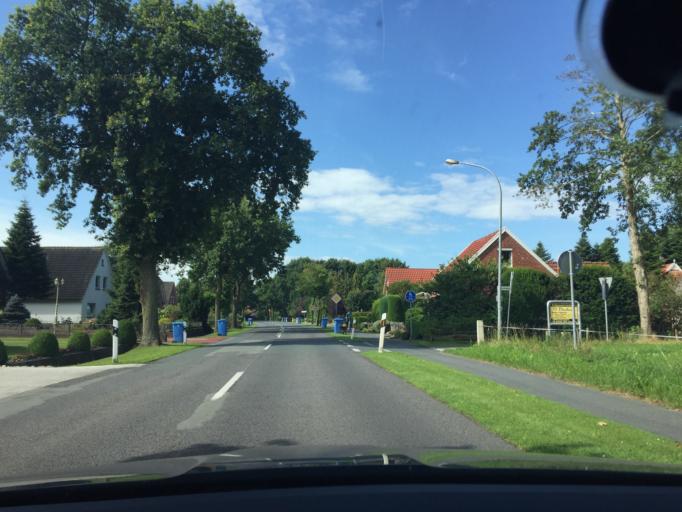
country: DE
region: Lower Saxony
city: Rechtsupweg
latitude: 53.5108
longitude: 7.3643
